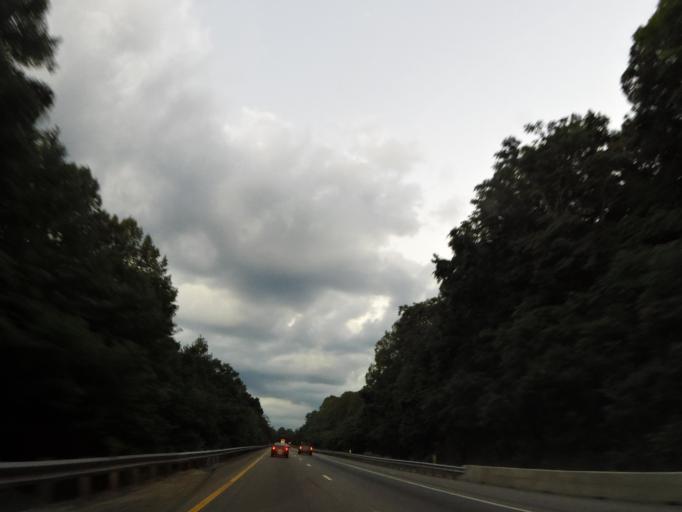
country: US
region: Tennessee
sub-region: Putnam County
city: Algood
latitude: 36.1421
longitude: -85.3783
